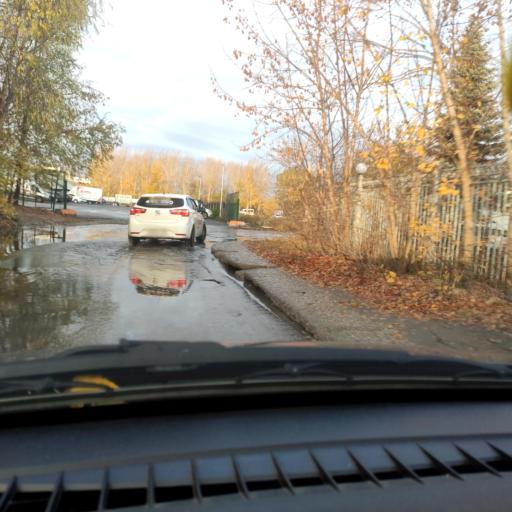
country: RU
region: Samara
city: Tol'yatti
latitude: 53.5384
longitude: 49.2870
